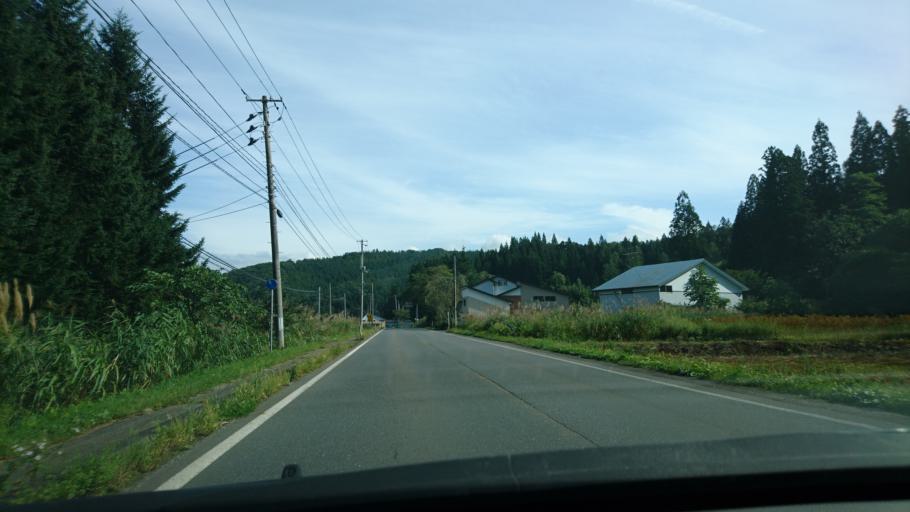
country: JP
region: Akita
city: Yokotemachi
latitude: 39.3131
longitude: 140.7579
